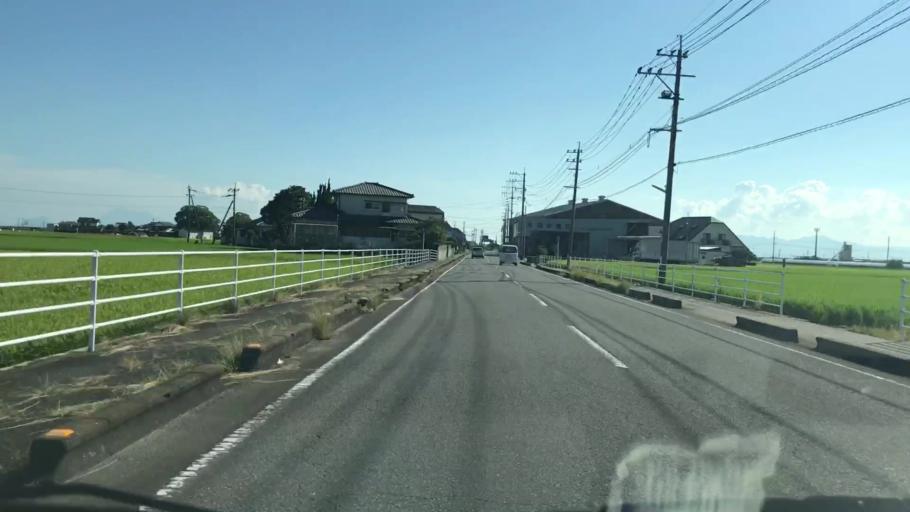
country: JP
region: Saga Prefecture
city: Okawa
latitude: 33.1950
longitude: 130.3343
